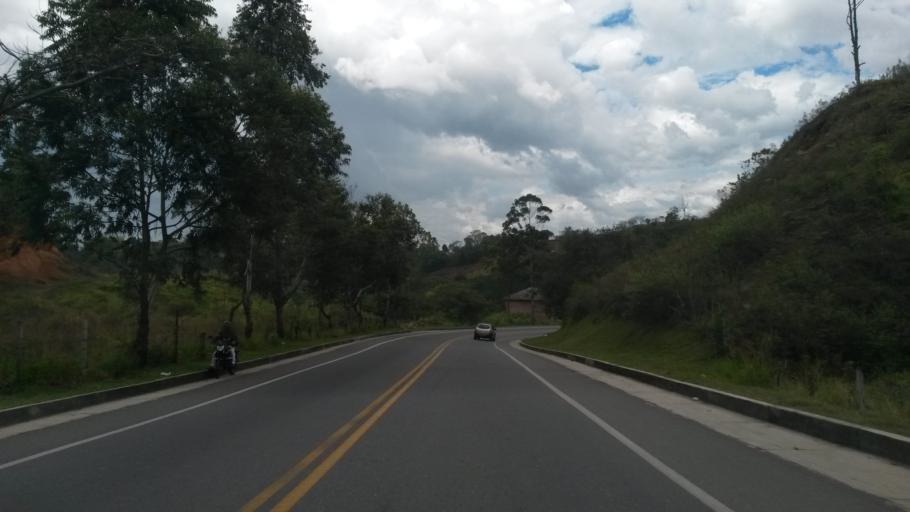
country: CO
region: Cauca
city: Popayan
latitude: 2.4229
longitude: -76.6313
